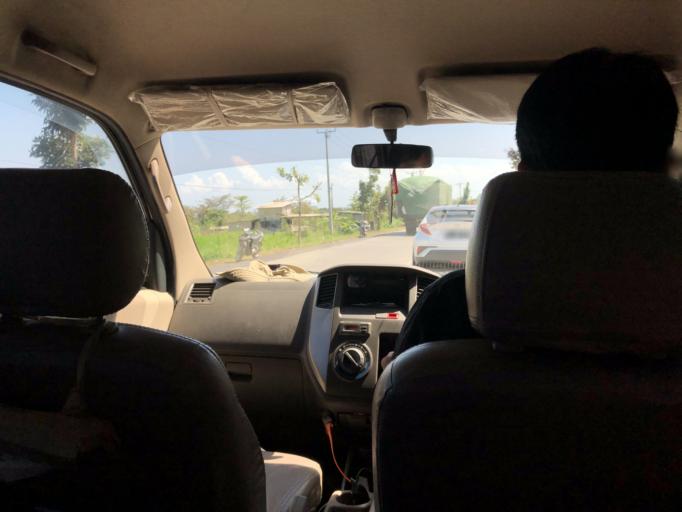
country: ID
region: Bali
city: Semarapura
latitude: -8.5696
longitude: 115.4059
